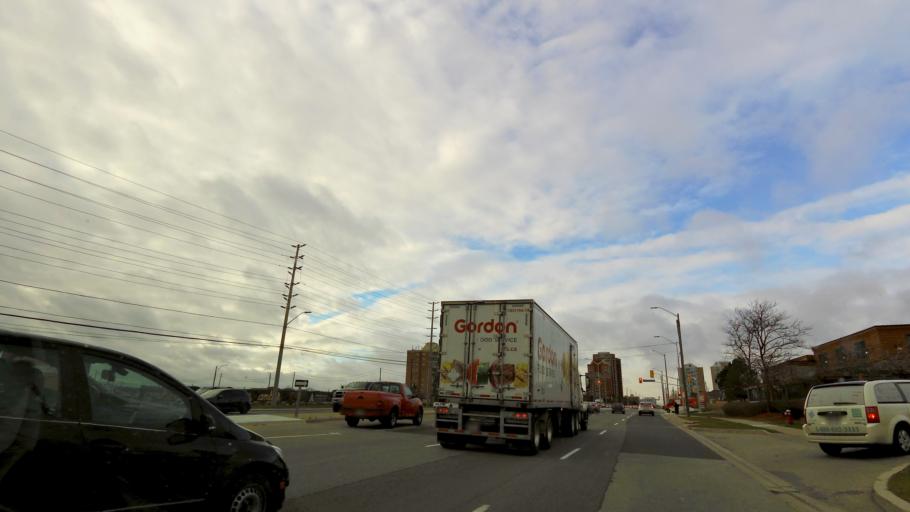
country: CA
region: Ontario
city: Mississauga
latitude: 43.6075
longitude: -79.6538
